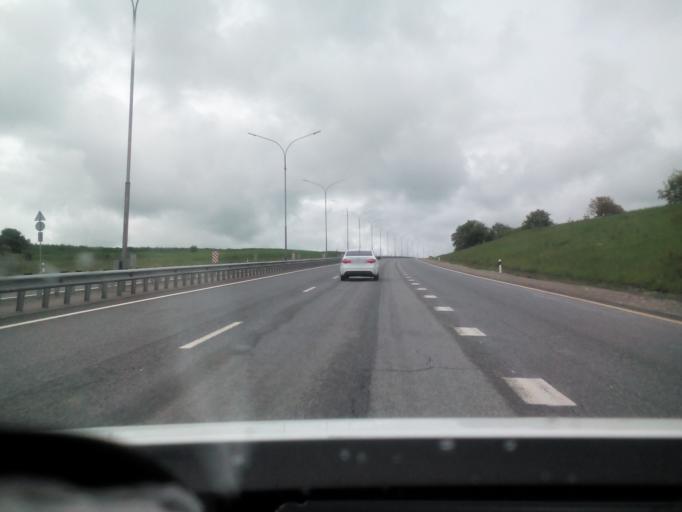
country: RU
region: Stavropol'skiy
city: Yessentuki
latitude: 44.0538
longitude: 42.8112
